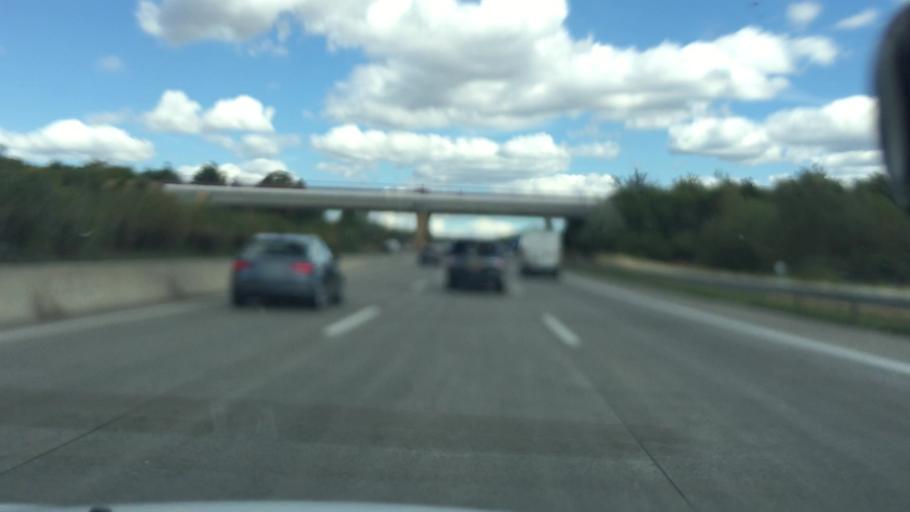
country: DE
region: Thuringia
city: Rockhausen
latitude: 50.9094
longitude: 11.0554
